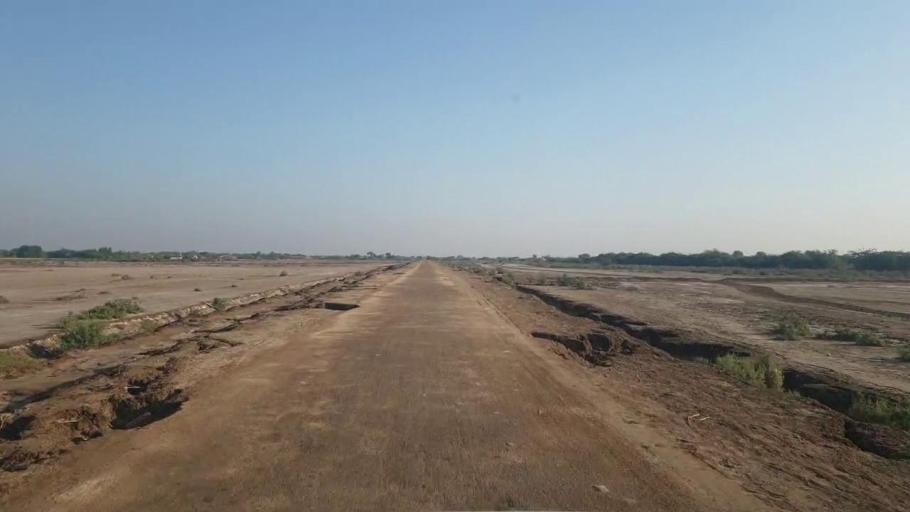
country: PK
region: Sindh
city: Badin
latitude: 24.7196
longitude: 68.8613
